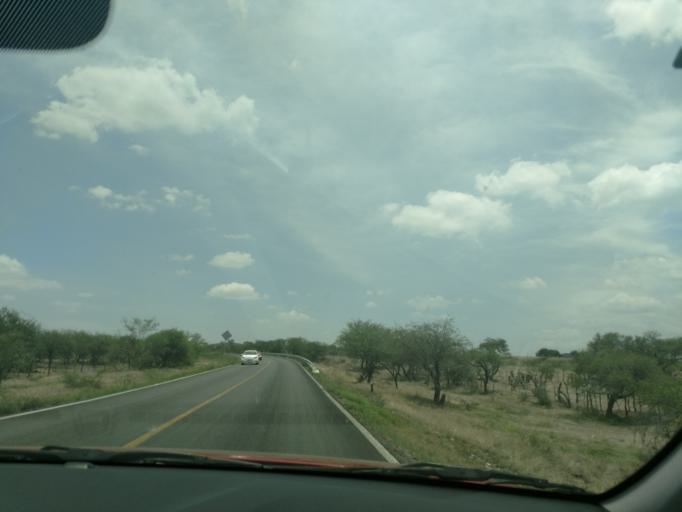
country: MX
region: San Luis Potosi
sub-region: Rioverde
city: Progreso
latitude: 22.0169
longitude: -100.3626
